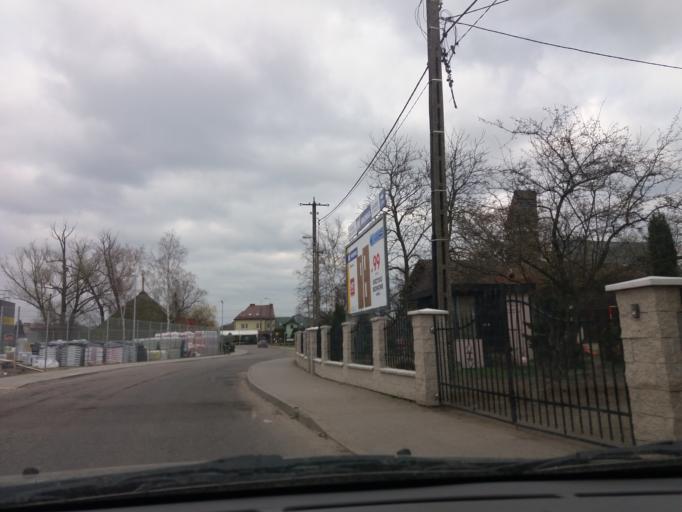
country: PL
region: Masovian Voivodeship
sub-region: Powiat mlawski
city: Mlawa
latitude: 53.1282
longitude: 20.3532
